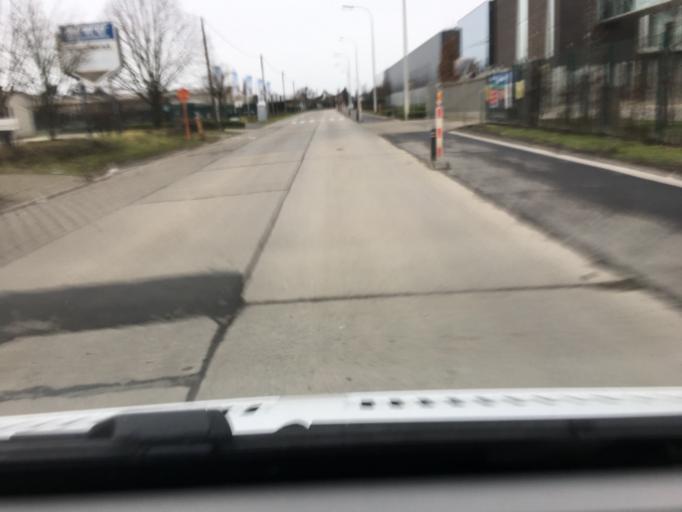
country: BE
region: Flanders
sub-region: Provincie West-Vlaanderen
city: Menen
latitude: 50.7889
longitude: 3.1052
